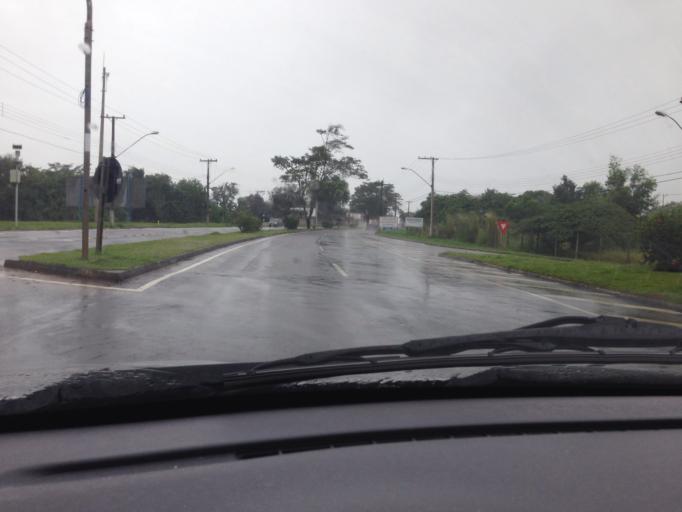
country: BR
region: Espirito Santo
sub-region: Guarapari
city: Guarapari
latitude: -20.6329
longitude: -40.5188
